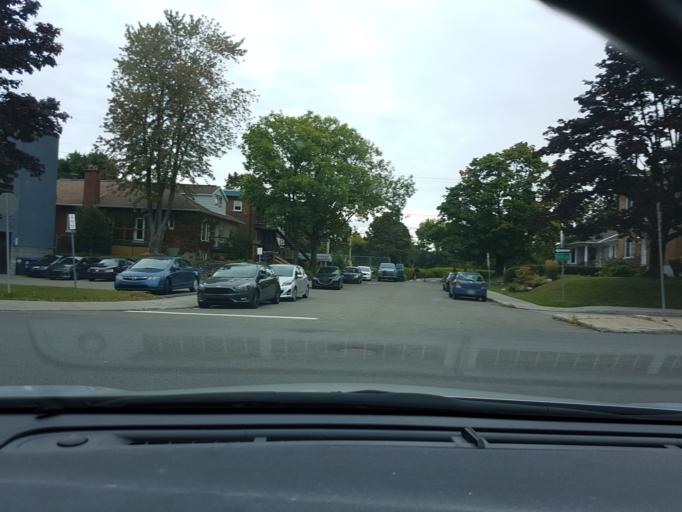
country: CA
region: Quebec
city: Quebec
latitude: 46.7908
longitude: -71.2627
